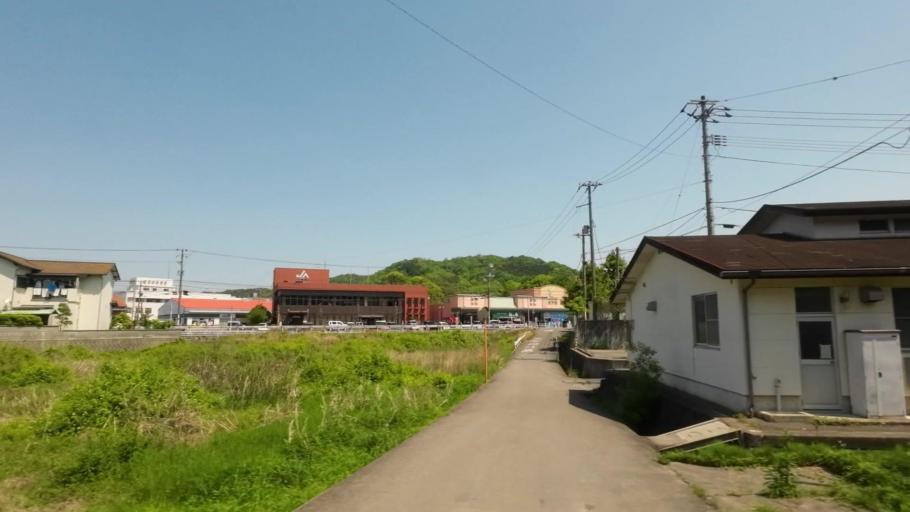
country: JP
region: Ehime
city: Hojo
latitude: 34.0973
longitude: 132.9504
